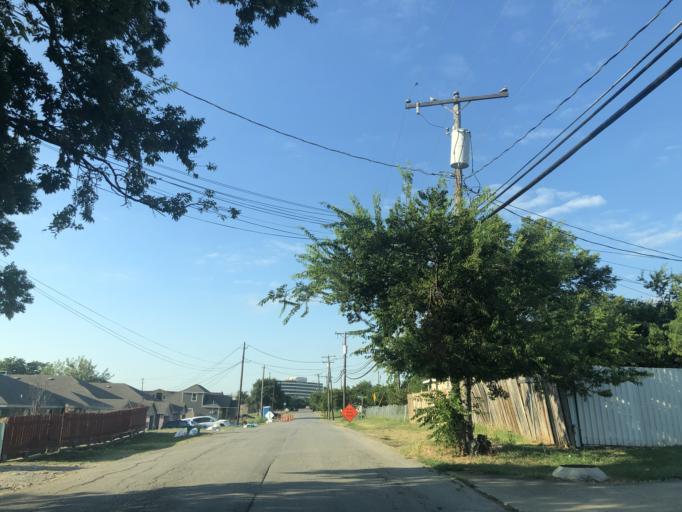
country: US
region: Texas
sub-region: Dallas County
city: Grand Prairie
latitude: 32.7464
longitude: -97.0188
